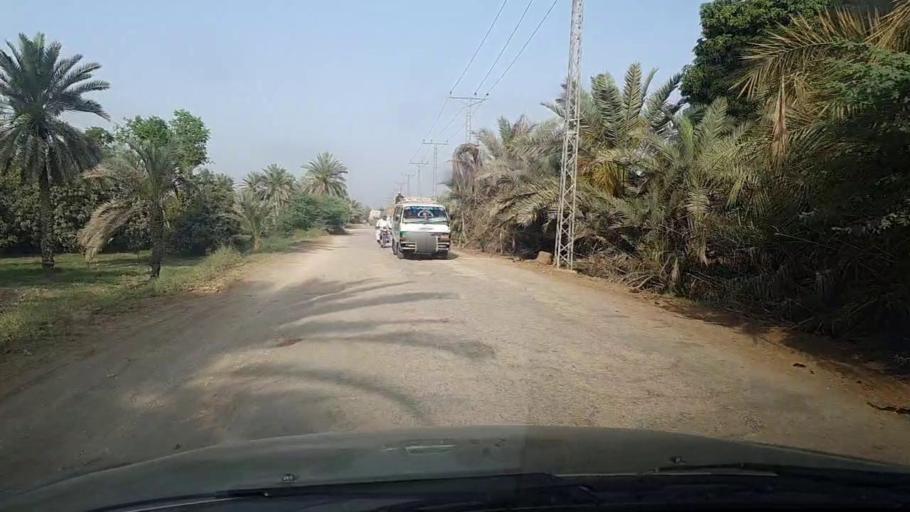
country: PK
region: Sindh
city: Pir jo Goth
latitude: 27.5718
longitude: 68.6195
